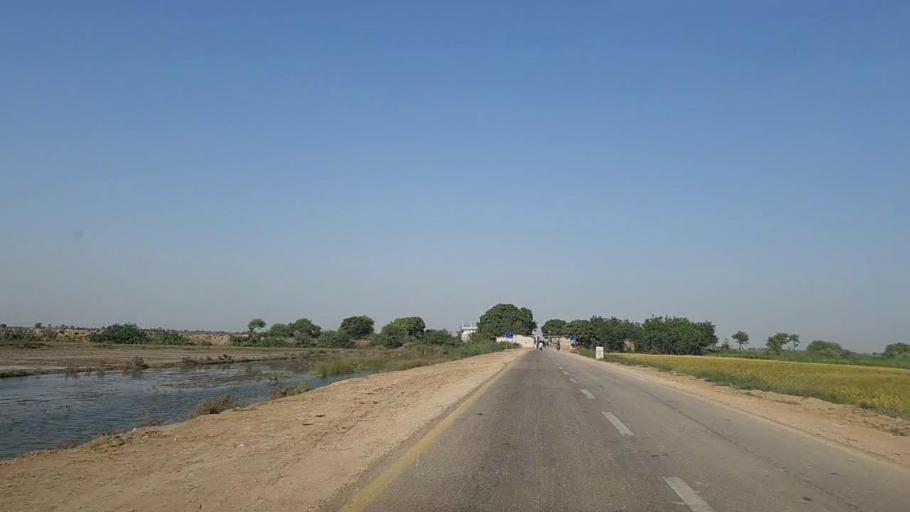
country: PK
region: Sindh
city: Jati
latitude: 24.4144
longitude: 68.3021
